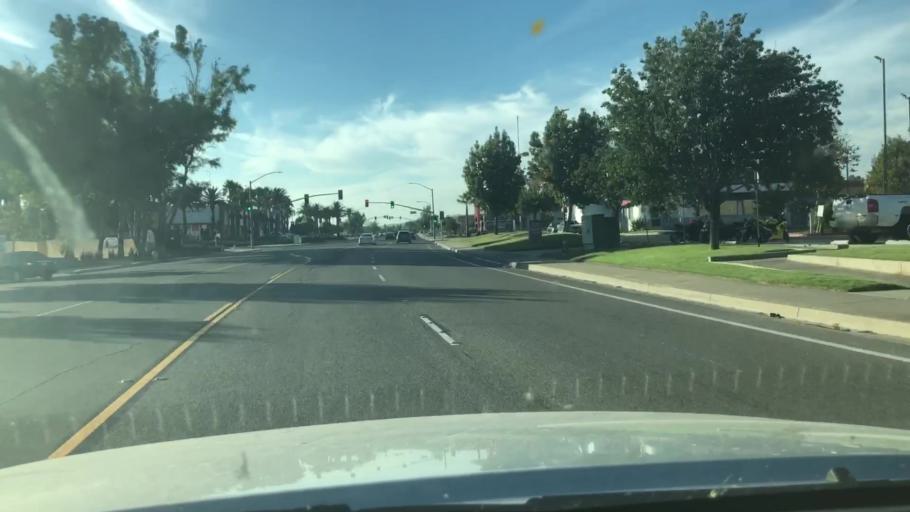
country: US
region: California
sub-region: Riverside County
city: Murrieta Hot Springs
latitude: 33.5287
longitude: -117.1745
